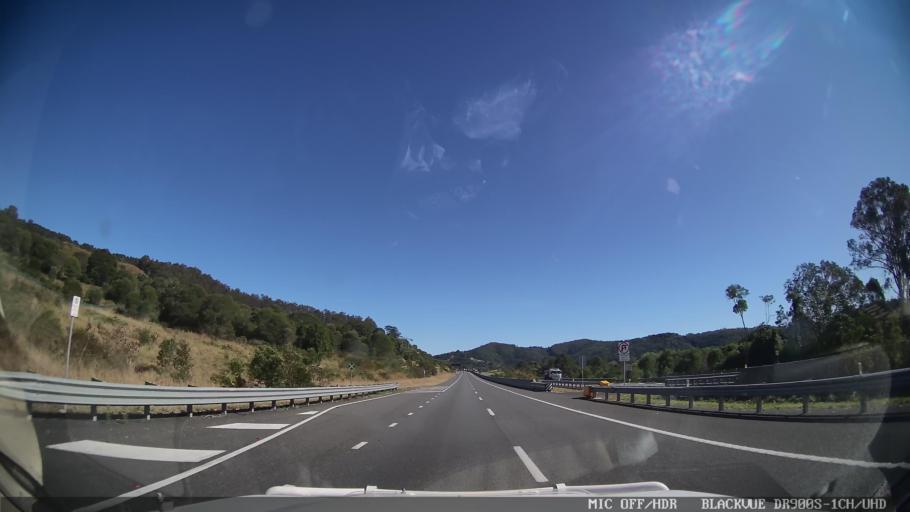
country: AU
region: Queensland
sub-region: Sunshine Coast
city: Black Mountain
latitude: -26.3929
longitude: 152.8145
